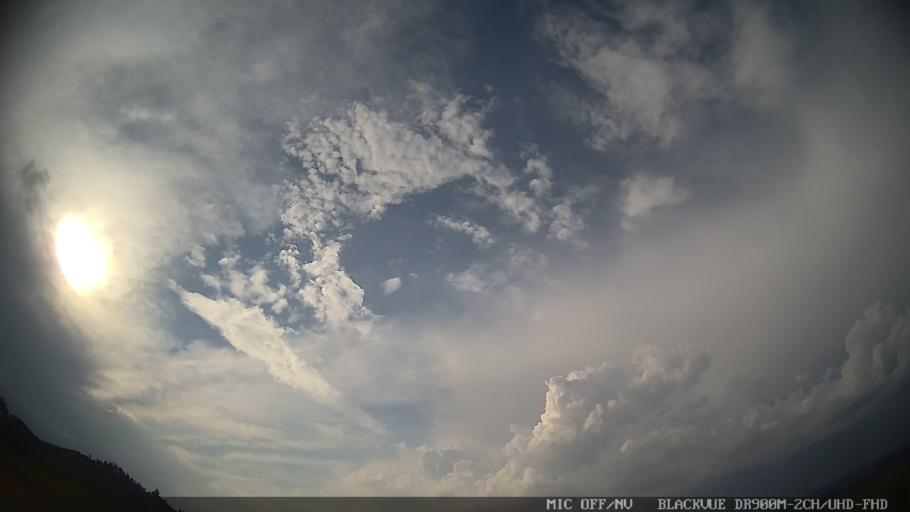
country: BR
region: Sao Paulo
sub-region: Braganca Paulista
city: Braganca Paulista
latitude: -22.9169
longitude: -46.5652
